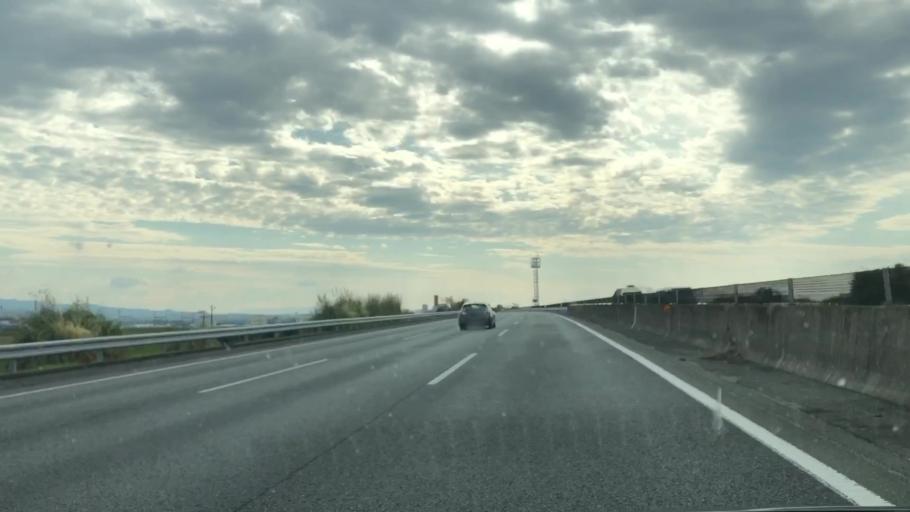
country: JP
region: Saga Prefecture
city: Tosu
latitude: 33.3563
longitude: 130.5387
